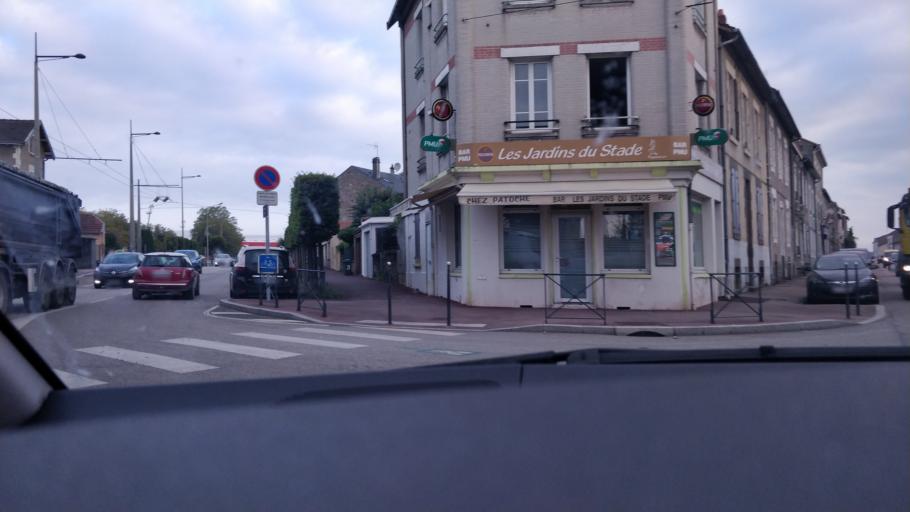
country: FR
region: Limousin
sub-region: Departement de la Haute-Vienne
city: Limoges
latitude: 45.8451
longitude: 1.2455
